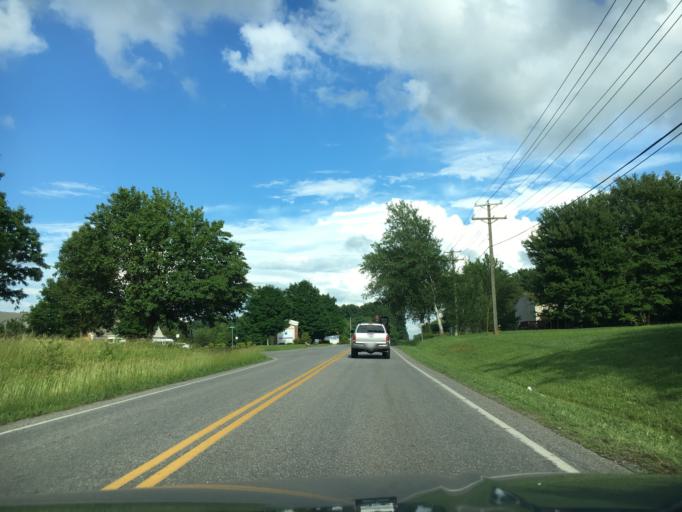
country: US
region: Virginia
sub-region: Campbell County
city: Timberlake
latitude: 37.3378
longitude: -79.2741
